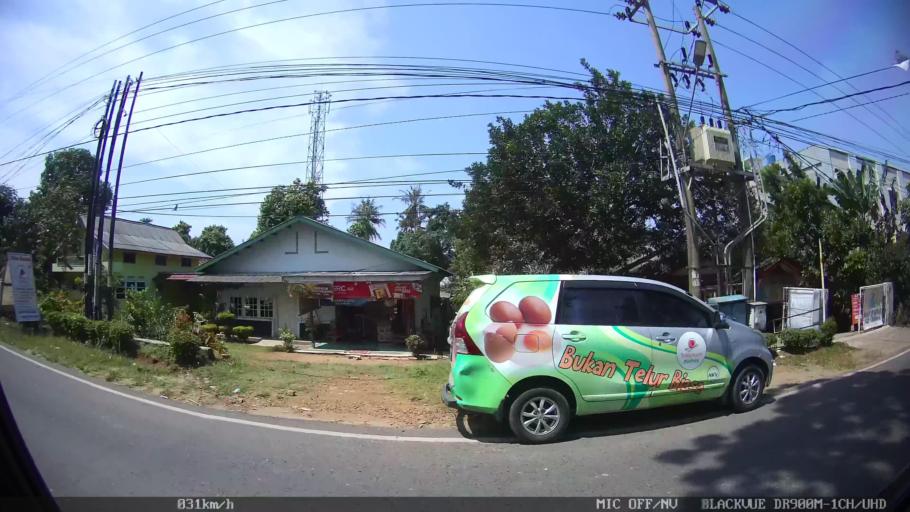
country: ID
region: Lampung
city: Kedaton
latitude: -5.3895
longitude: 105.2719
